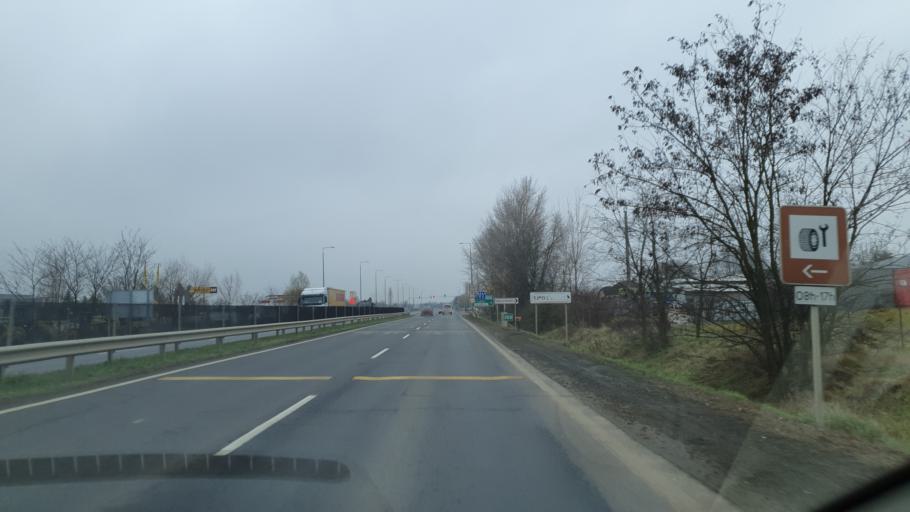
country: HU
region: Szabolcs-Szatmar-Bereg
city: Nyiregyhaza
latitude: 47.9042
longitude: 21.7123
